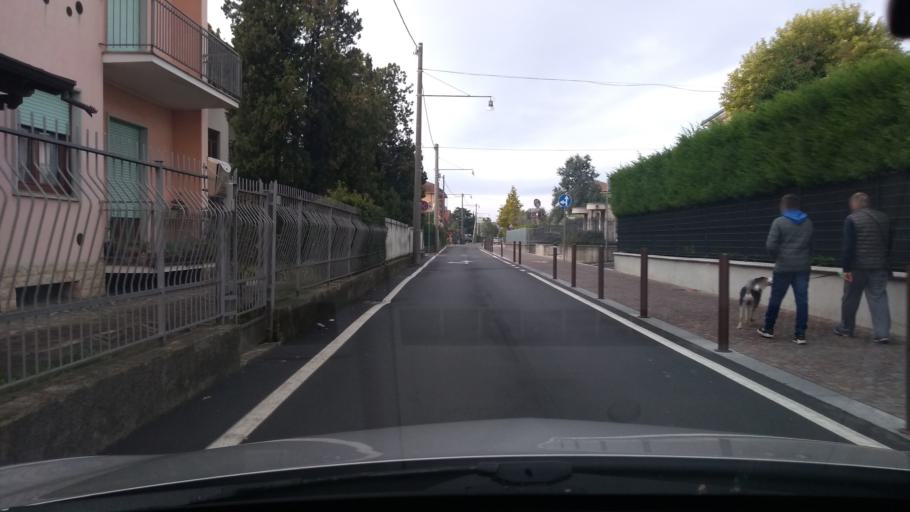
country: IT
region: Lombardy
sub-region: Provincia di Bergamo
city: Verdellino
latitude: 45.6026
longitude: 9.6134
